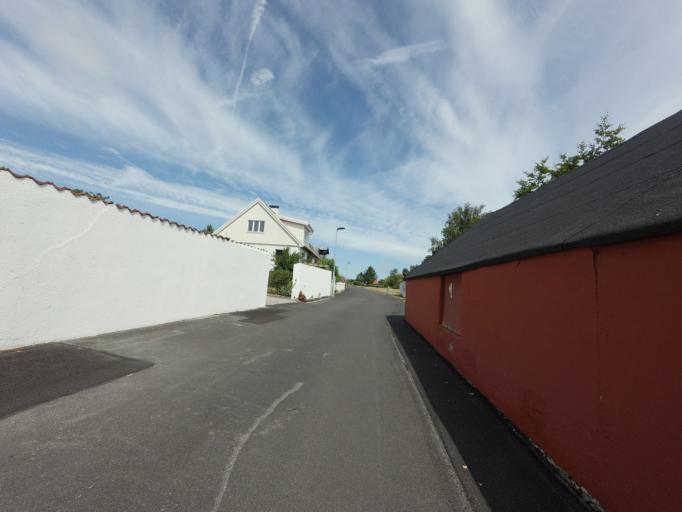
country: SE
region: Skane
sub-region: Simrishamns Kommun
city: Simrishamn
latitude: 55.5441
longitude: 14.3571
